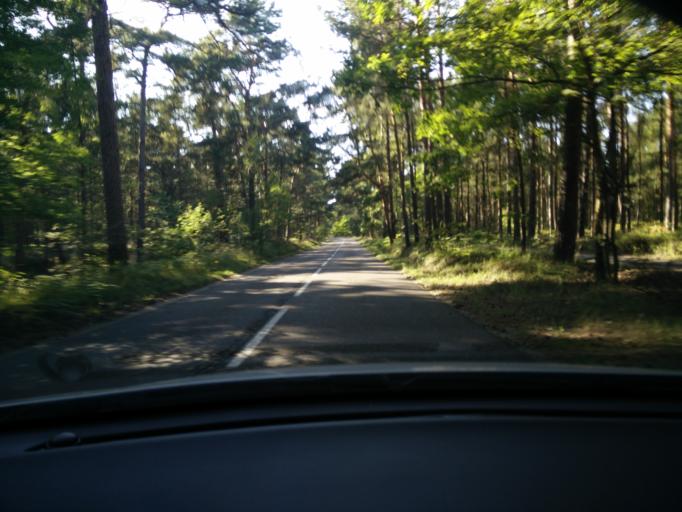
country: PL
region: Pomeranian Voivodeship
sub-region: Powiat pucki
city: Jastarnia
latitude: 54.6687
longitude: 18.7410
